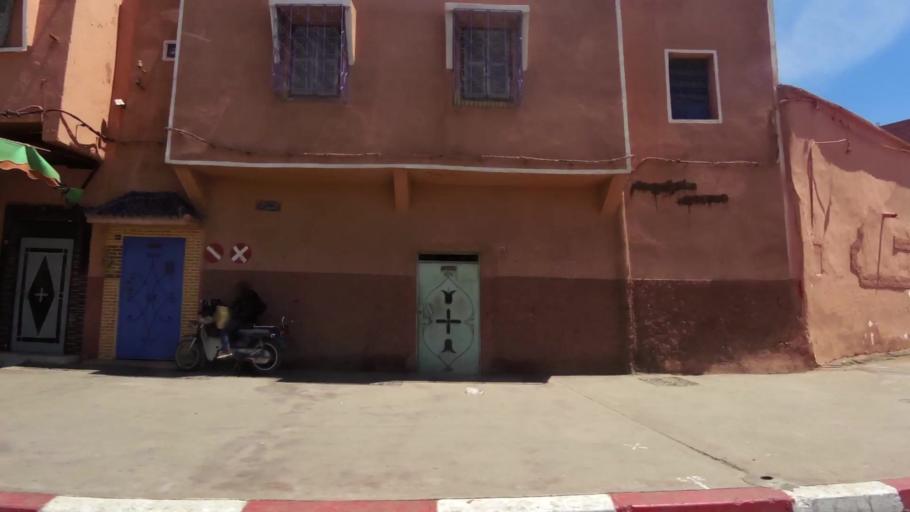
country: MA
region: Marrakech-Tensift-Al Haouz
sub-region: Marrakech
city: Marrakesh
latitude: 31.6195
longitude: -7.9718
